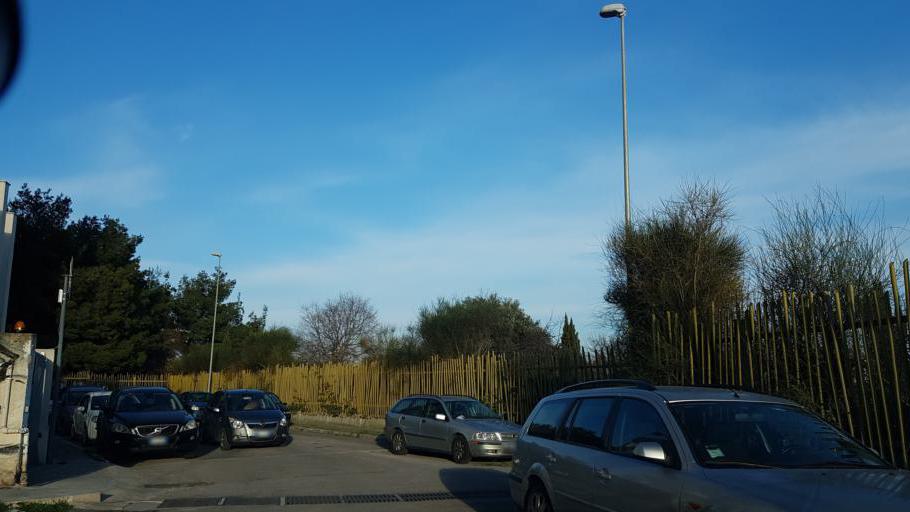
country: IT
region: Apulia
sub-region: Provincia di Brindisi
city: Brindisi
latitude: 40.6276
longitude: 17.9385
